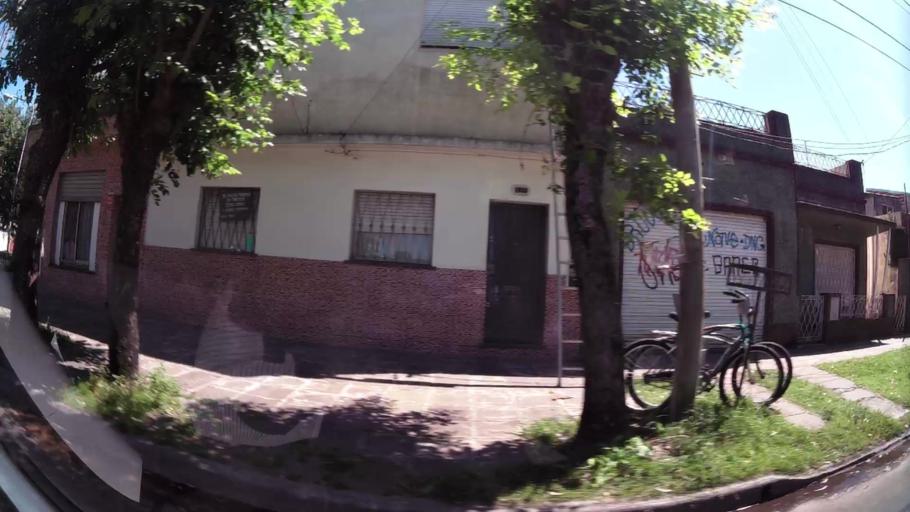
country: AR
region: Buenos Aires
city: Hurlingham
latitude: -34.5036
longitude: -58.6242
